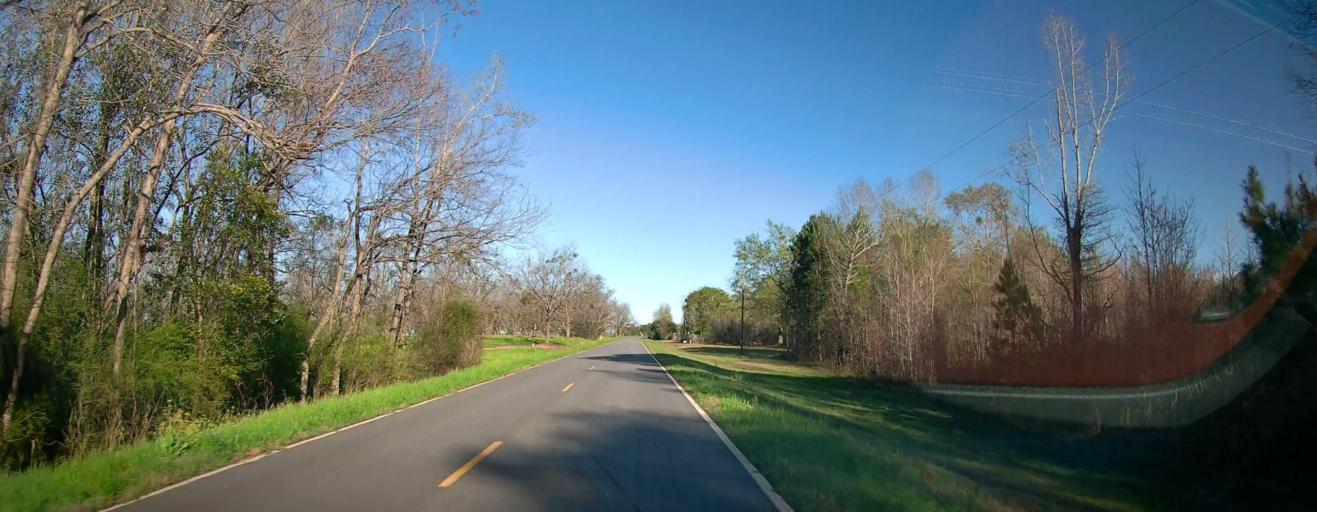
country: US
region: Georgia
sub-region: Pulaski County
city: Hawkinsville
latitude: 32.3474
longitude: -83.5813
